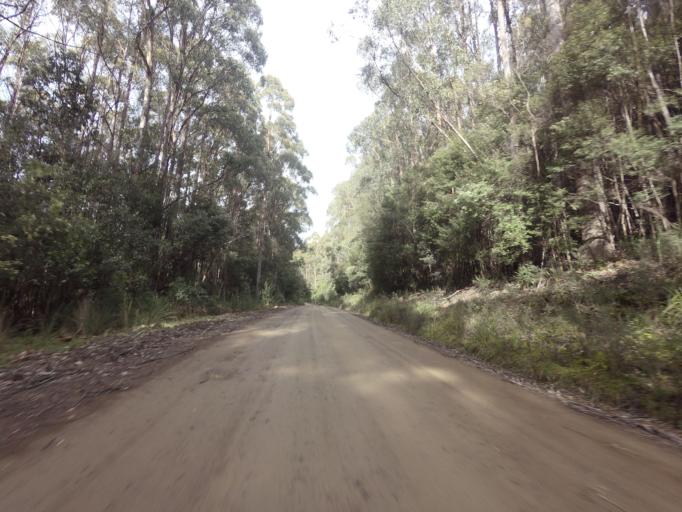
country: AU
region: Tasmania
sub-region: Huon Valley
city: Geeveston
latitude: -43.4834
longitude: 146.8924
